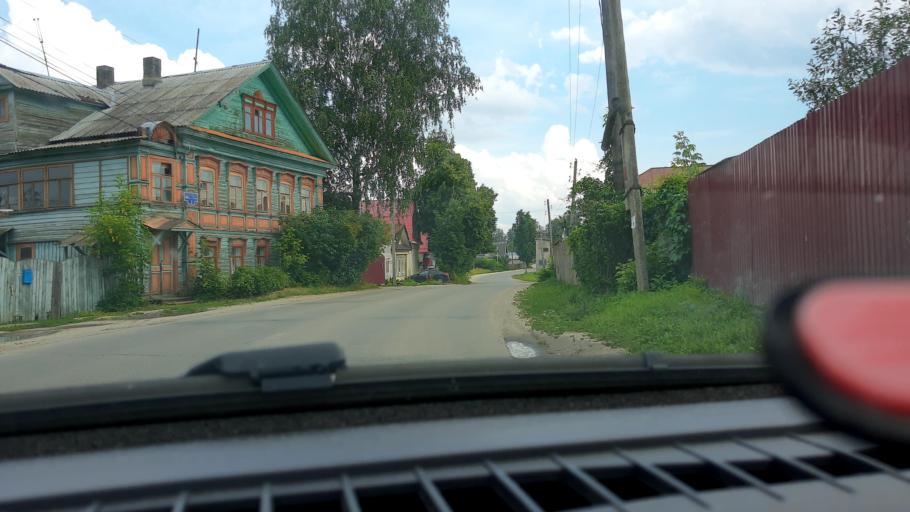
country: RU
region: Nizjnij Novgorod
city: Gorodets
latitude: 56.6379
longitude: 43.4743
